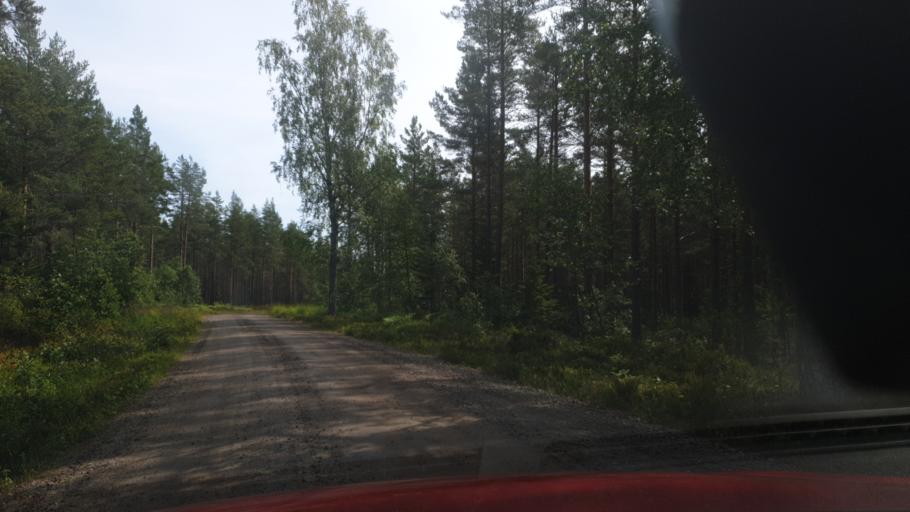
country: SE
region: Gaevleborg
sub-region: Hudiksvalls Kommun
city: Hudiksvall
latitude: 61.6420
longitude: 17.4651
